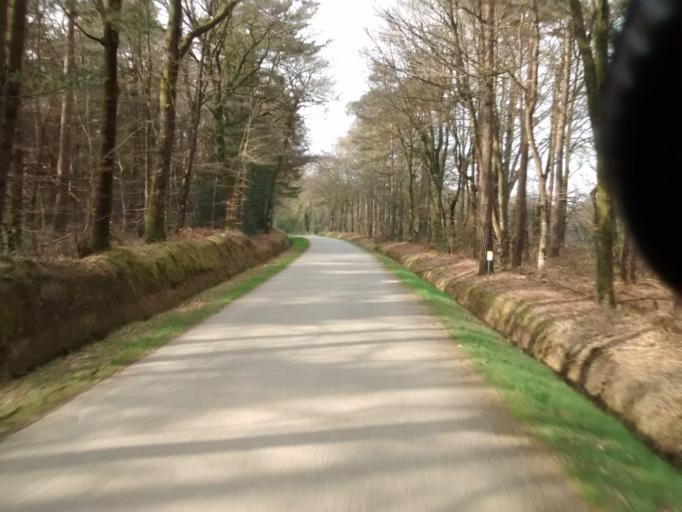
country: FR
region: Brittany
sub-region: Departement des Cotes-d'Armor
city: Merdrignac
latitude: 48.1270
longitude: -2.3879
